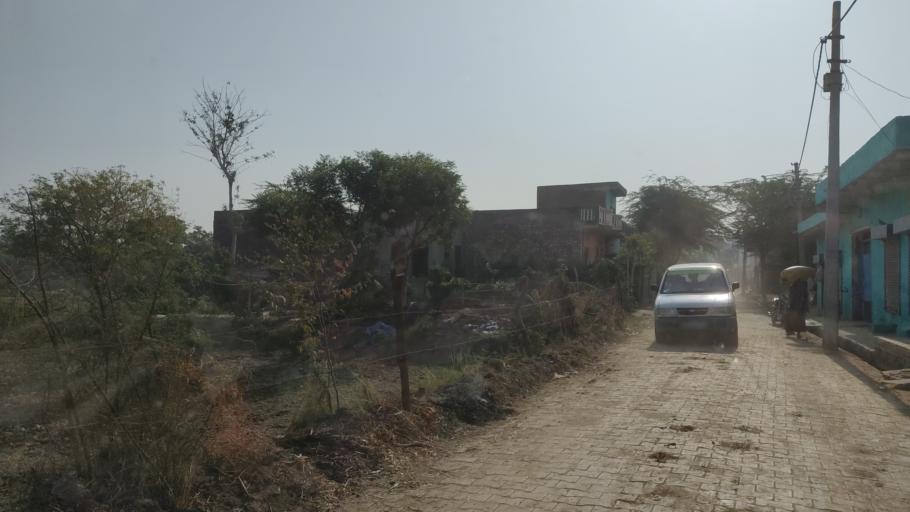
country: IN
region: Uttar Pradesh
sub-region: Mathura
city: Radha Kund
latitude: 27.5605
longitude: 77.5585
